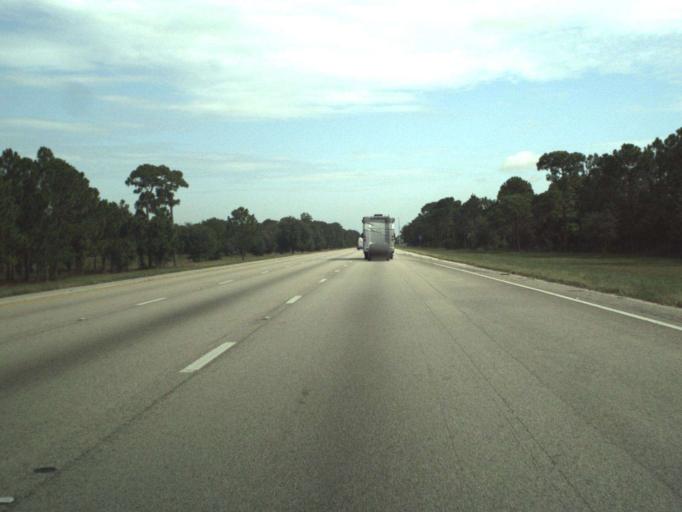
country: US
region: Florida
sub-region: Martin County
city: Palm City
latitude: 27.1678
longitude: -80.3919
